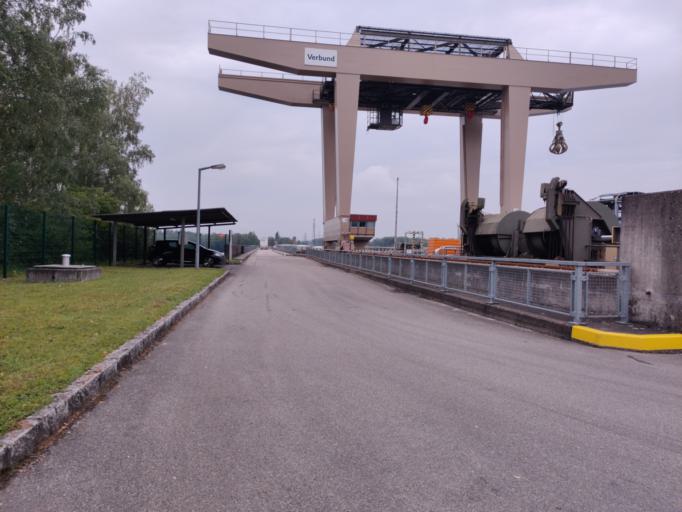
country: AT
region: Upper Austria
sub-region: Politischer Bezirk Linz-Land
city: Asten
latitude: 48.2508
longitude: 14.4333
